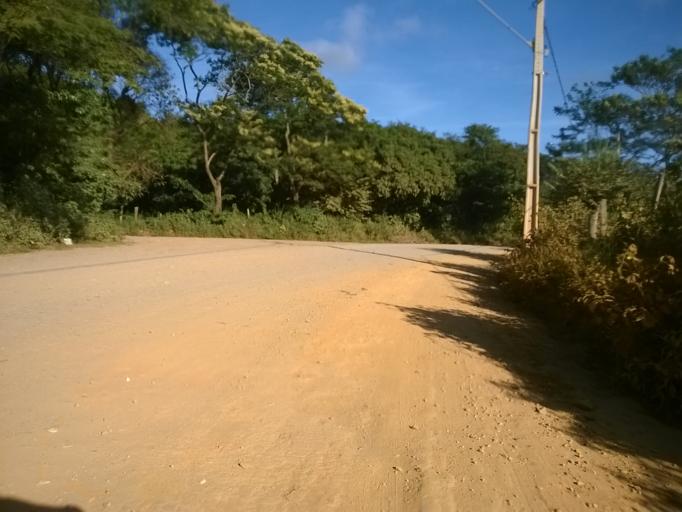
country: BR
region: Minas Gerais
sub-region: Uba
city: Uba
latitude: -21.0869
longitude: -42.9803
